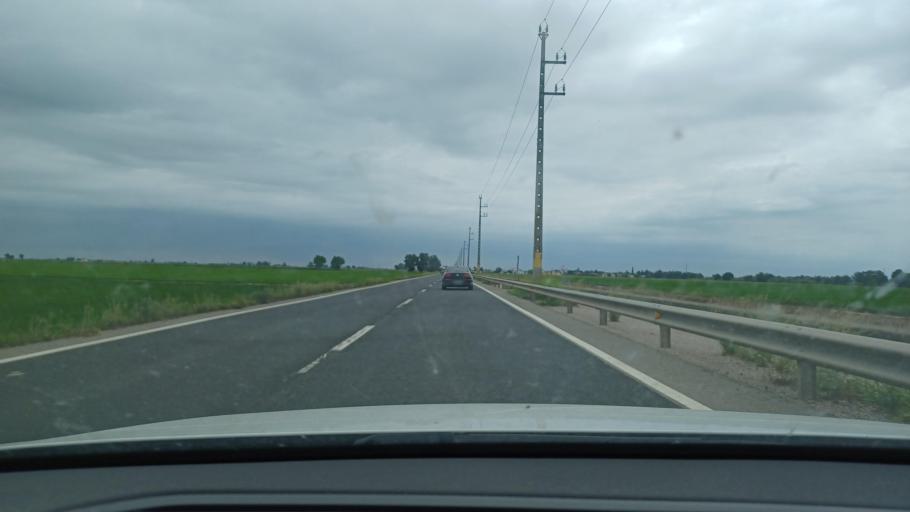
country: ES
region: Catalonia
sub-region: Provincia de Tarragona
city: Deltebre
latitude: 40.7240
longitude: 0.6638
